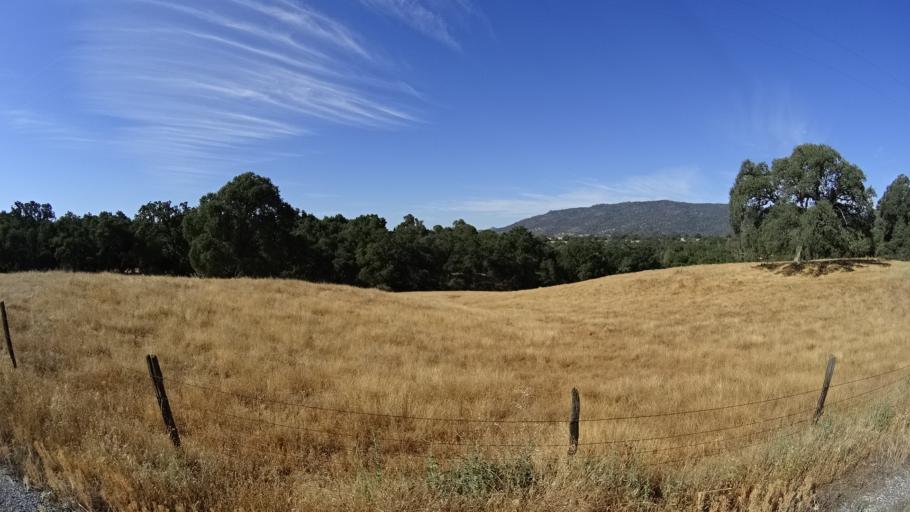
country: US
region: California
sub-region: Calaveras County
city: San Andreas
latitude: 38.1755
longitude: -120.6483
